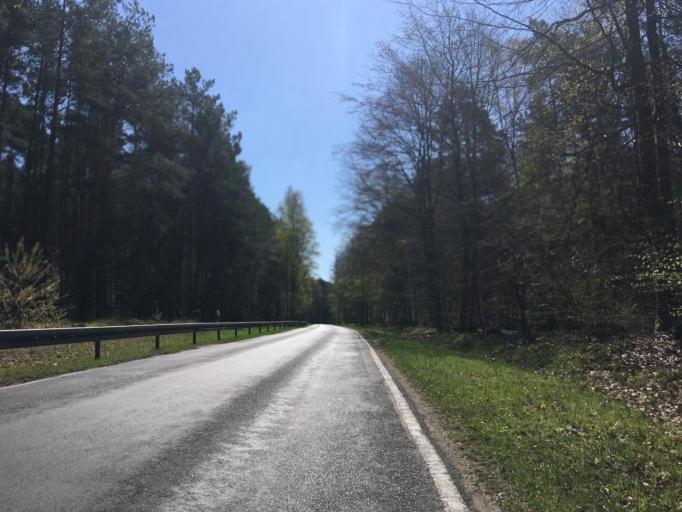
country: DE
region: Brandenburg
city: Bernau bei Berlin
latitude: 52.7146
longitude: 13.5768
